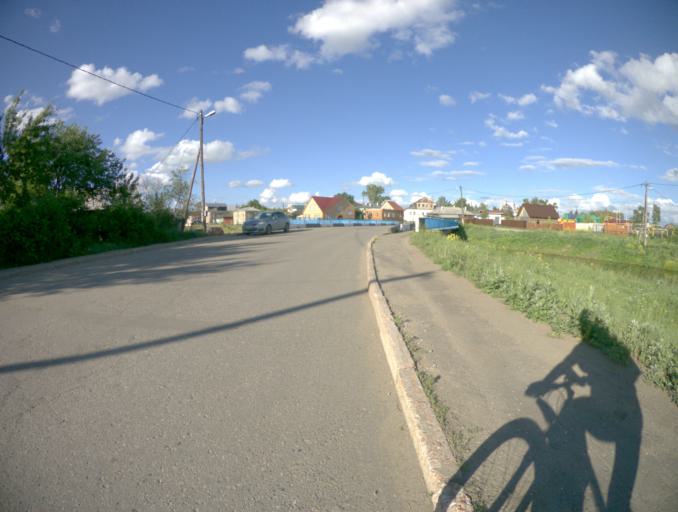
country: RU
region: Vladimir
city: Yur'yev-Pol'skiy
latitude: 56.4975
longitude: 39.6744
